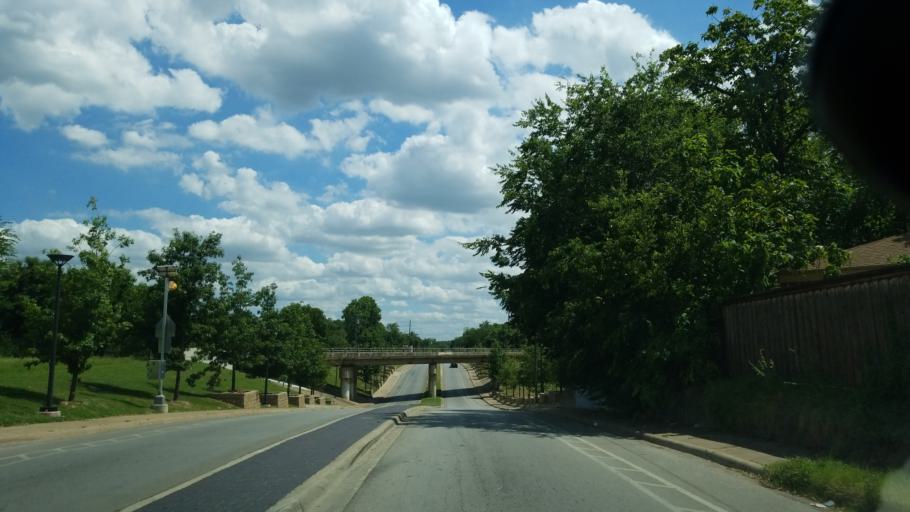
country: US
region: Texas
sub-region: Dallas County
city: Dallas
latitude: 32.7447
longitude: -96.7534
